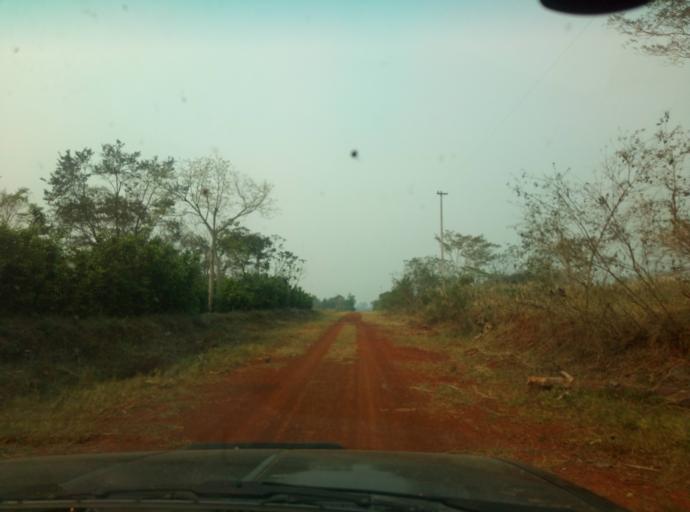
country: PY
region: Caaguazu
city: Carayao
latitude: -25.2062
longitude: -56.2241
